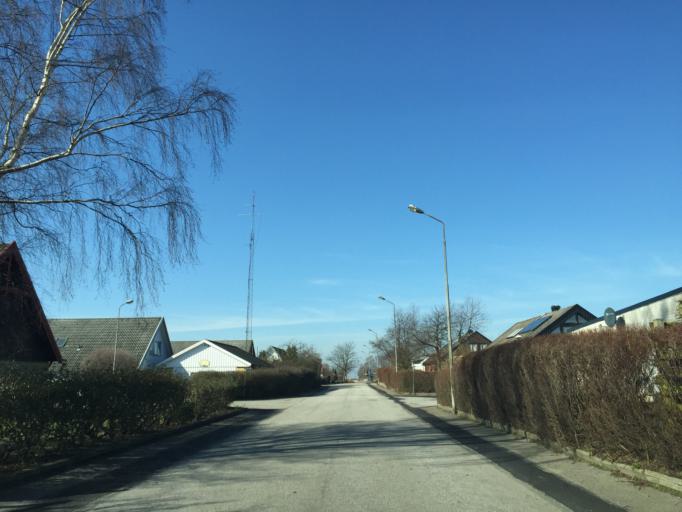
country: SE
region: Skane
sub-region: Staffanstorps Kommun
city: Hjaerup
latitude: 55.6687
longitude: 13.1368
